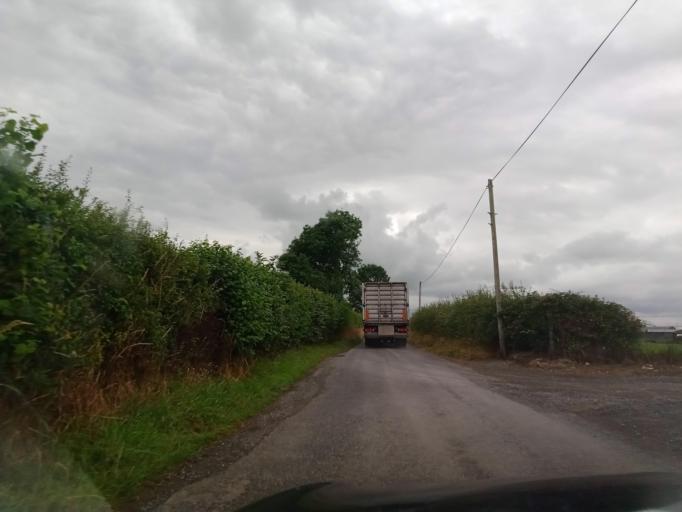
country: IE
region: Leinster
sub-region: Laois
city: Stradbally
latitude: 52.9609
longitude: -7.1792
